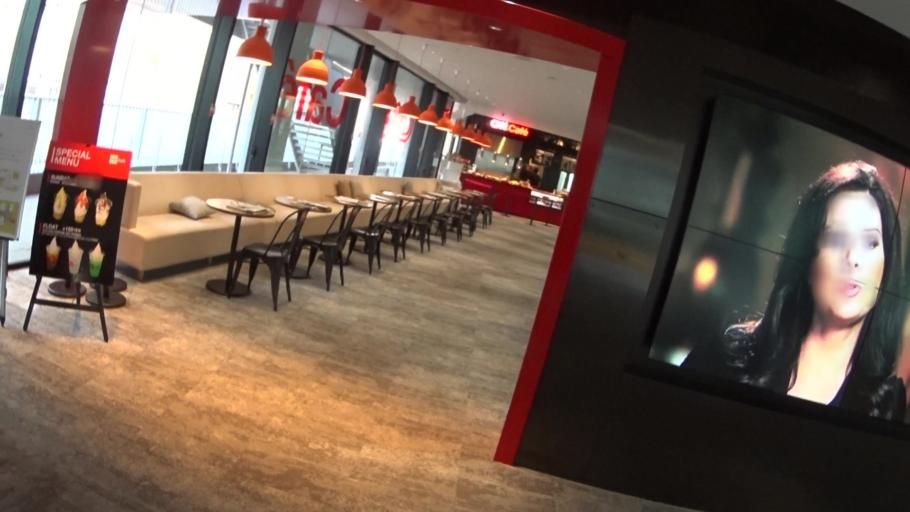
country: JP
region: Osaka
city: Yao
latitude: 34.6505
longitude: 135.5874
